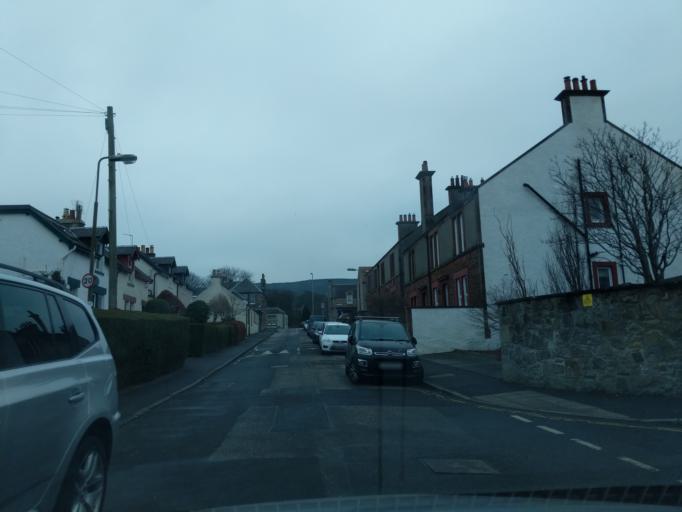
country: GB
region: Scotland
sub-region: Edinburgh
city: Currie
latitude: 55.9027
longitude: -3.2897
